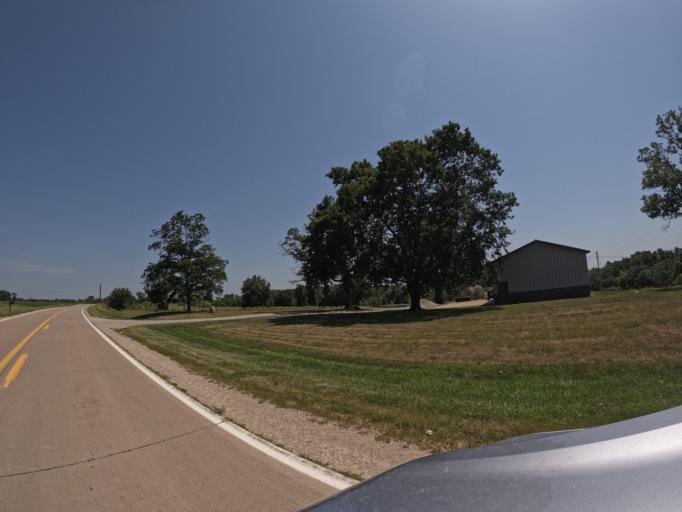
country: US
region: Iowa
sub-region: Henry County
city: Mount Pleasant
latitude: 40.9857
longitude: -91.6359
